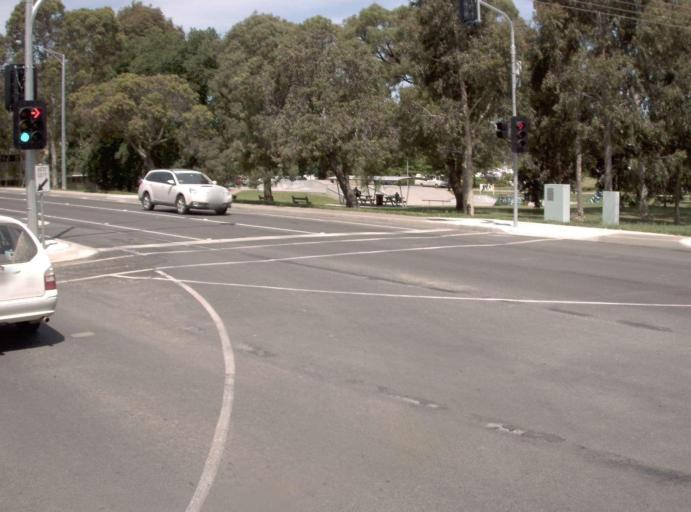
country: AU
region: Victoria
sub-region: Wellington
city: Sale
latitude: -38.1116
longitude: 147.0612
